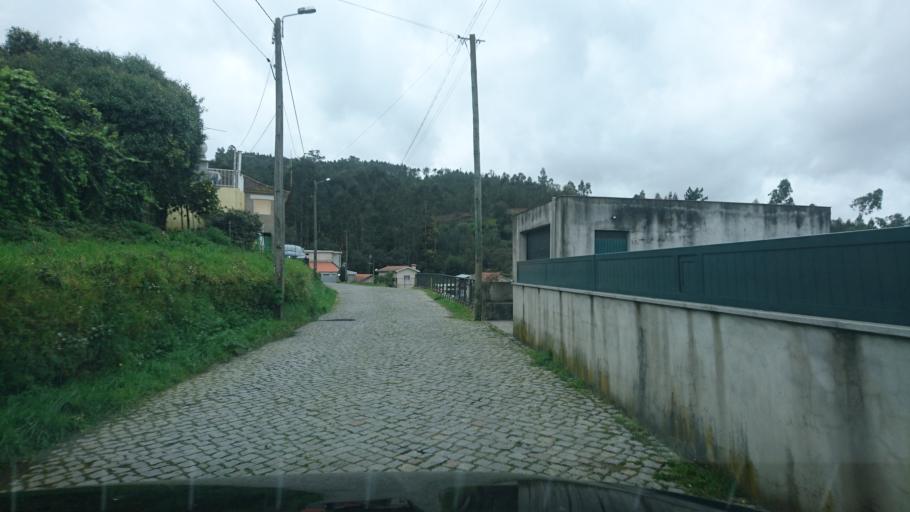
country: PT
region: Porto
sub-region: Paredes
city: Recarei
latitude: 41.1387
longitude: -8.3946
